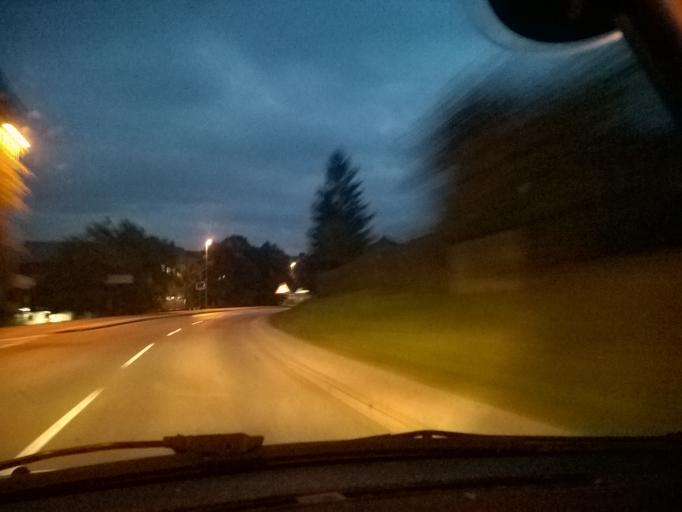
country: SI
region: Rogaska Slatina
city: Rogaska Slatina
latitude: 46.2261
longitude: 15.6456
